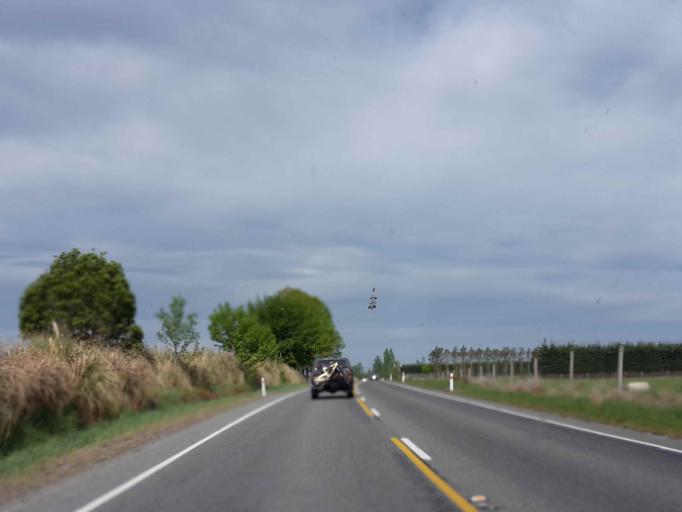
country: NZ
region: Canterbury
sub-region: Timaru District
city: Pleasant Point
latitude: -44.1185
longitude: 171.1814
